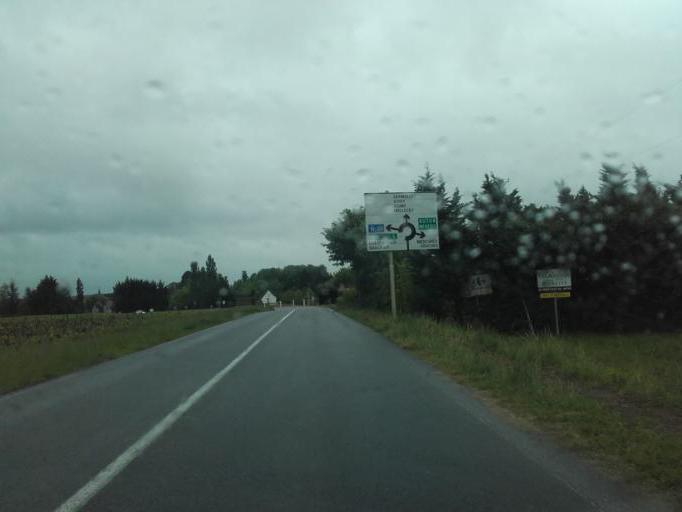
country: FR
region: Bourgogne
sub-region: Departement de Saone-et-Loire
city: Dracy-le-Fort
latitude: 46.8180
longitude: 4.7519
